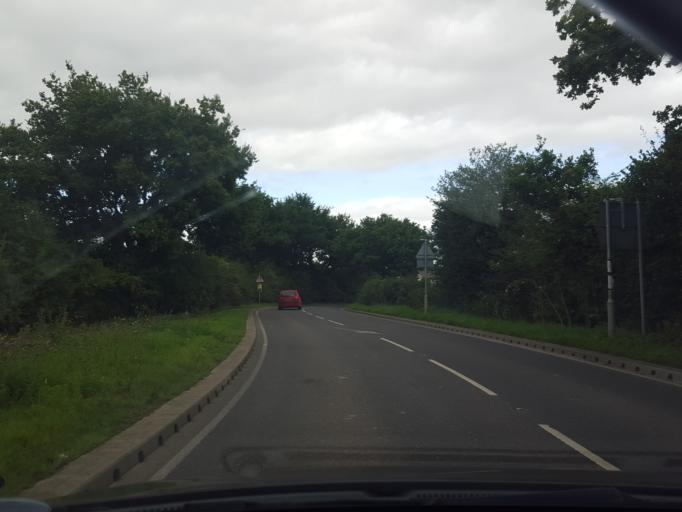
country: GB
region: England
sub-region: Essex
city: Great Bentley
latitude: 51.8500
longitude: 1.0357
